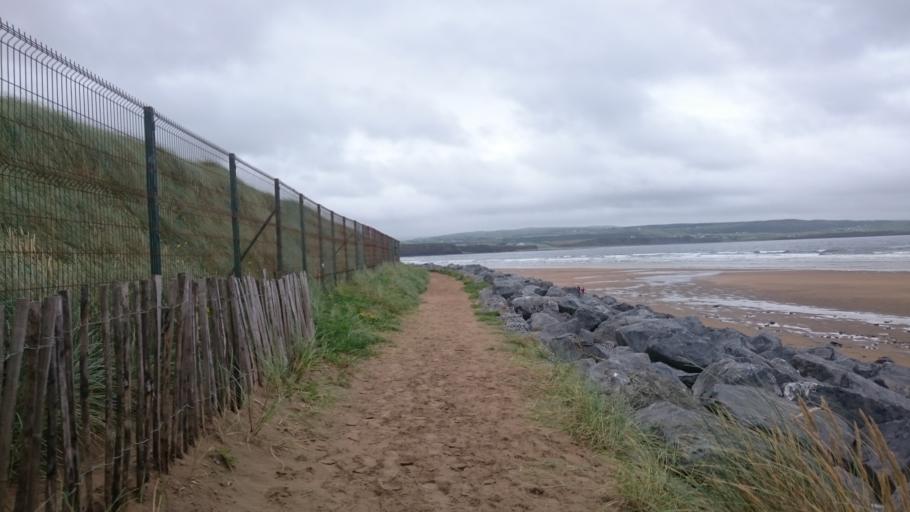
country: IE
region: Munster
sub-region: An Clar
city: Kilrush
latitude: 52.9398
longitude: -9.3569
